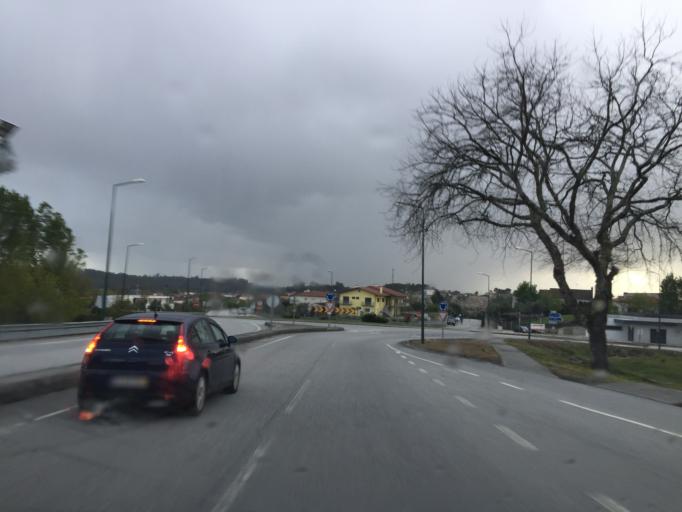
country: PT
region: Viseu
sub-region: Viseu
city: Viseu
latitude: 40.6170
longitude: -7.9553
